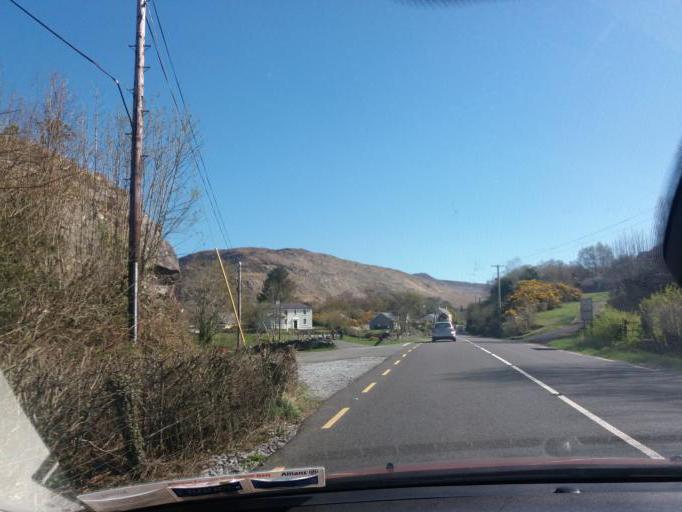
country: IE
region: Munster
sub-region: Ciarrai
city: Cill Airne
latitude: 51.9760
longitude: -9.3351
